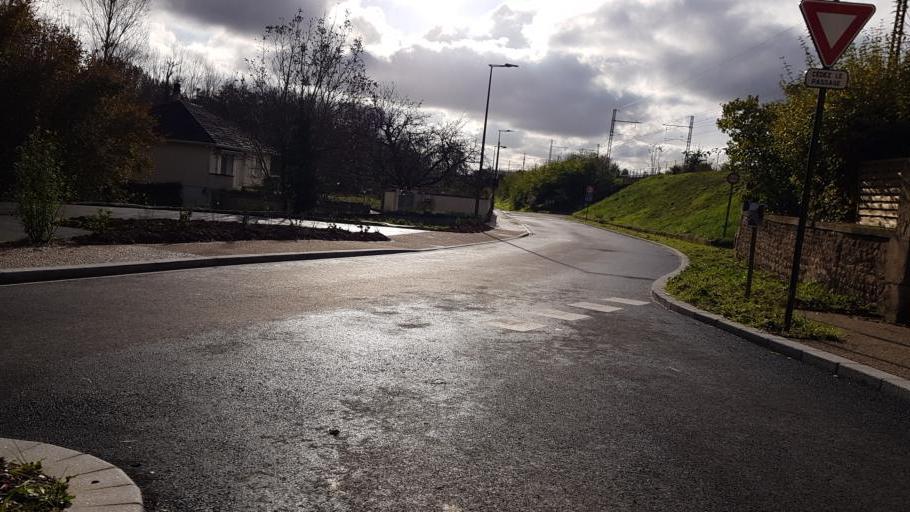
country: FR
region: Poitou-Charentes
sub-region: Departement de la Vienne
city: Chasseneuil-du-Poitou
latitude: 46.6467
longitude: 0.3696
